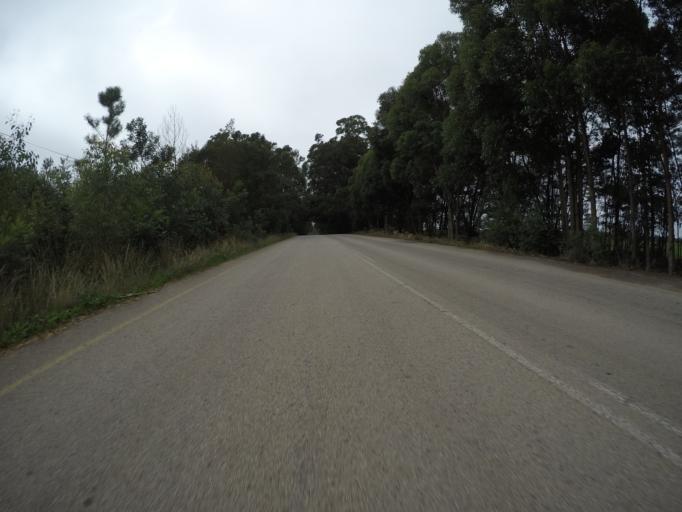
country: ZA
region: Eastern Cape
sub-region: Cacadu District Municipality
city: Kareedouw
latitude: -33.9969
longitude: 24.1548
